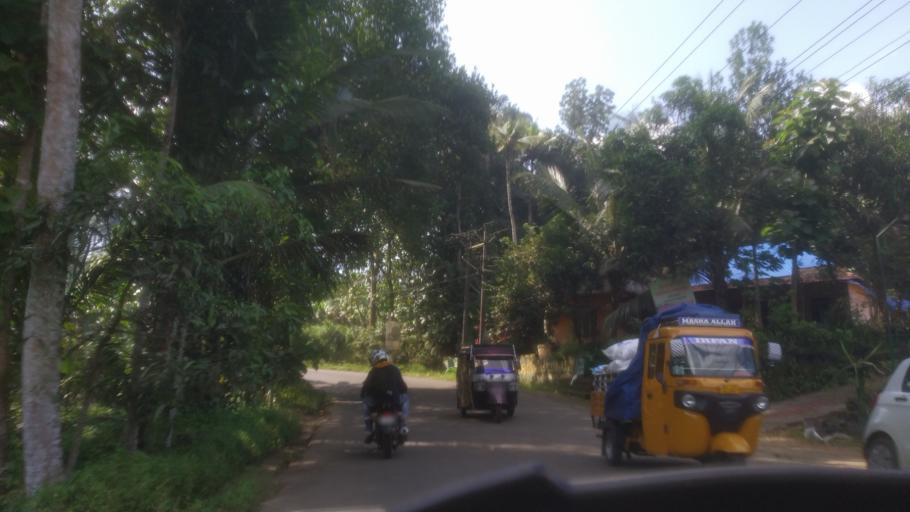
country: IN
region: Kerala
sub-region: Ernakulam
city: Muvattupula
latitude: 9.9996
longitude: 76.6308
